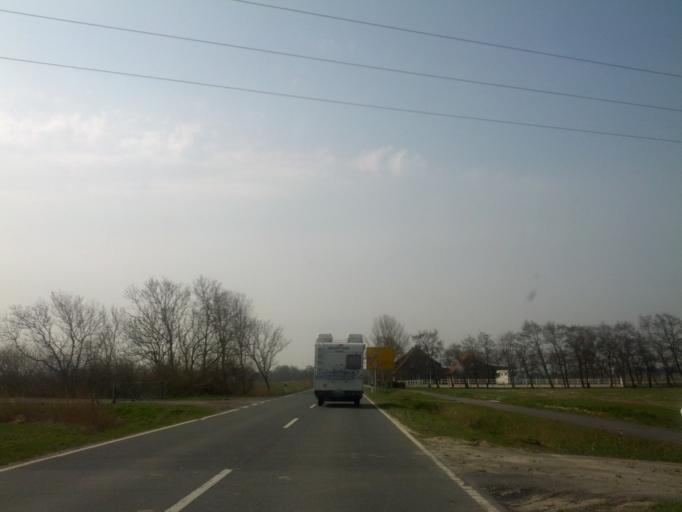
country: DE
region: Lower Saxony
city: Norddeich
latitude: 53.6164
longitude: 7.1872
